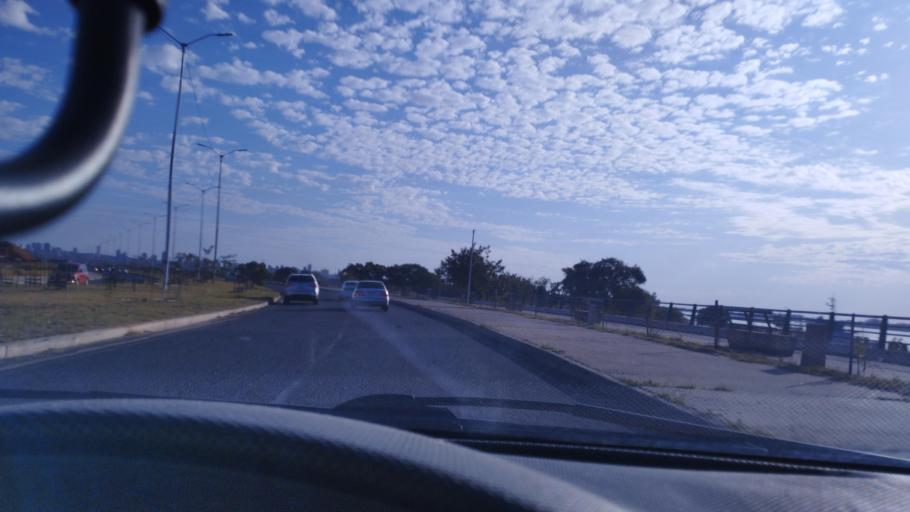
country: PY
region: Asuncion
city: Asuncion
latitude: -25.2495
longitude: -57.6040
